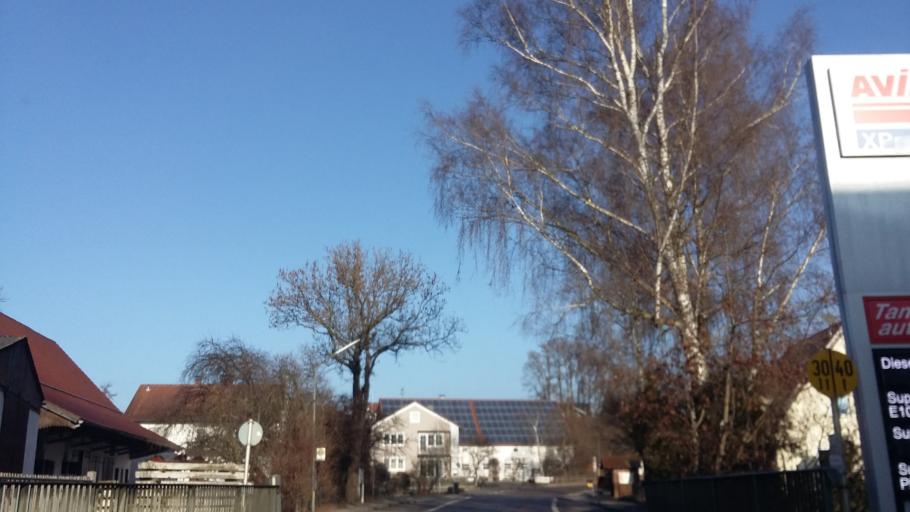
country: DE
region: Bavaria
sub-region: Swabia
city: Adelzhausen
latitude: 48.3563
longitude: 11.1377
